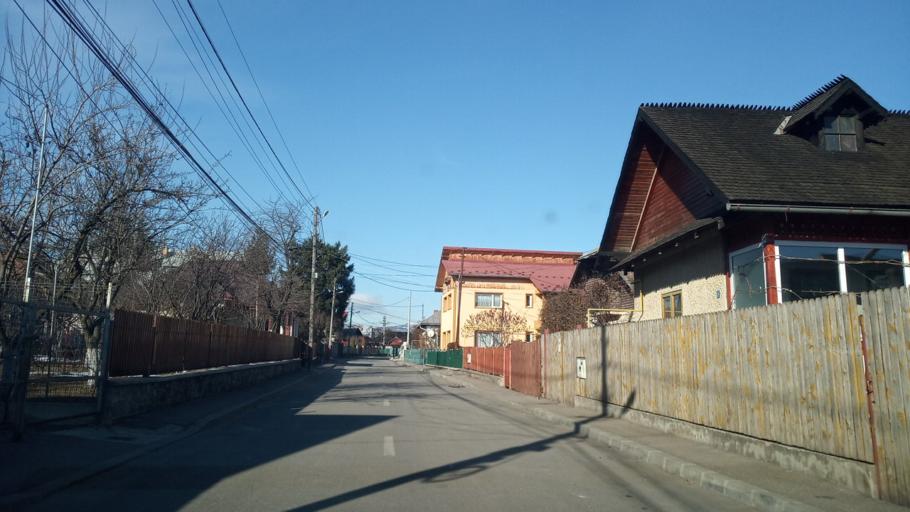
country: RO
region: Prahova
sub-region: Oras Breaza
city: Breaza
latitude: 45.1864
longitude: 25.6669
